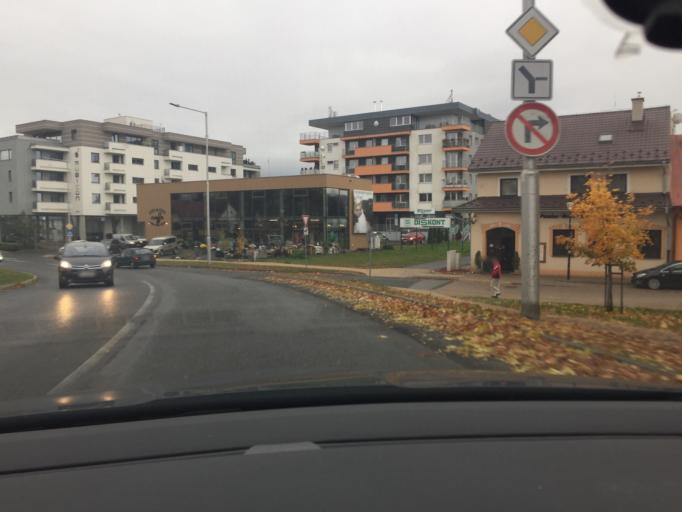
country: SK
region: Presovsky
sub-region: Okres Poprad
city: Poprad
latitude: 49.0675
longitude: 20.2799
